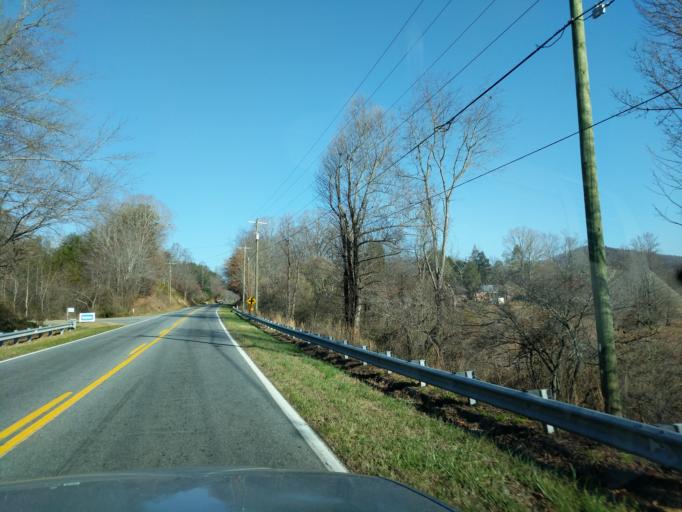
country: US
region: North Carolina
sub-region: McDowell County
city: West Marion
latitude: 35.6236
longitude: -81.9863
